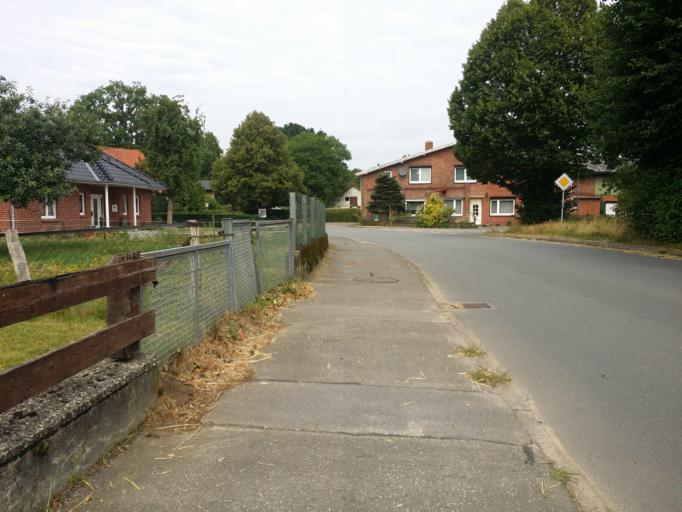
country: DE
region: Schleswig-Holstein
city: Huje
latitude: 53.9761
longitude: 9.4368
